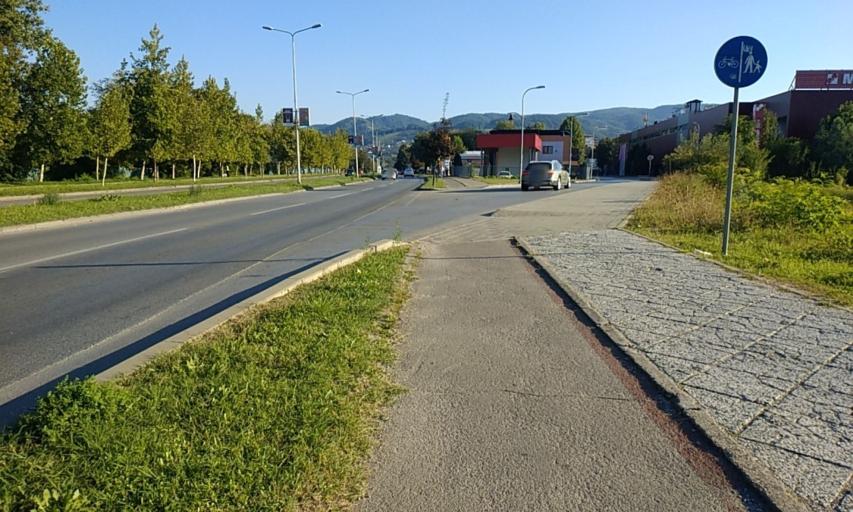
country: BA
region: Republika Srpska
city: Starcevica
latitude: 44.7772
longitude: 17.2064
